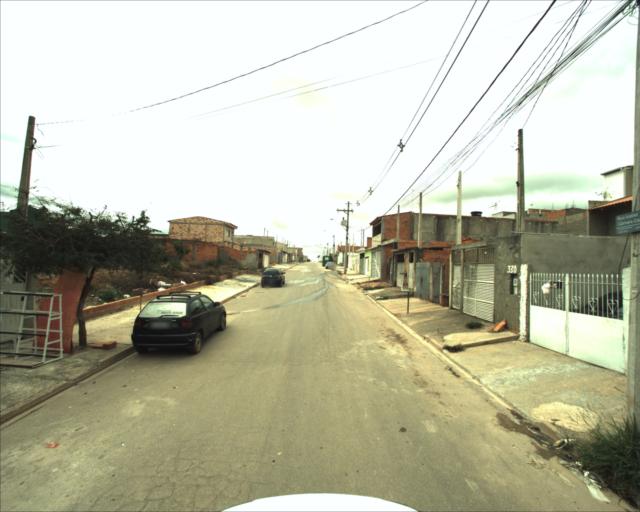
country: BR
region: Sao Paulo
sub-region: Sorocaba
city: Sorocaba
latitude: -23.4373
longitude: -47.5006
